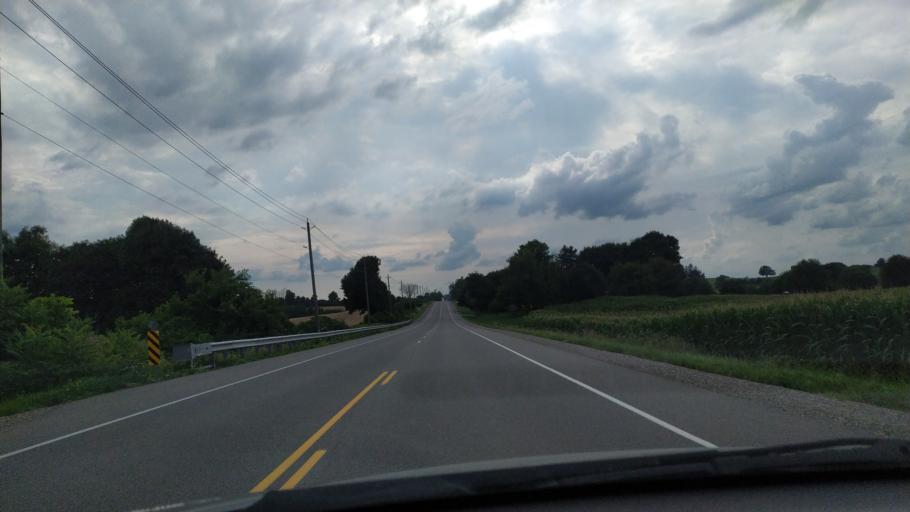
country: CA
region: Ontario
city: Kitchener
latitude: 43.3615
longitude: -80.4614
